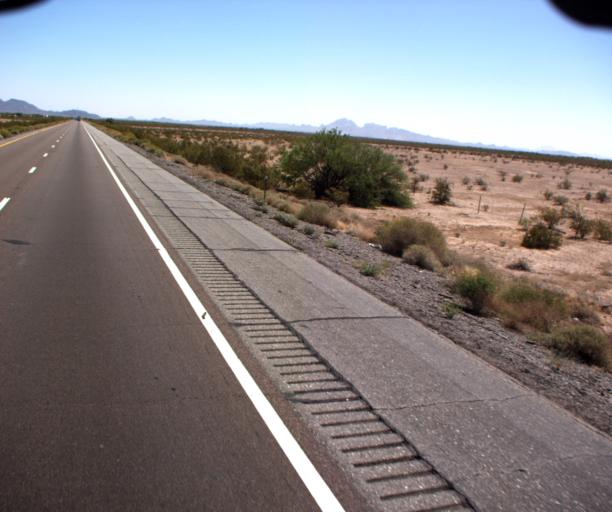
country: US
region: Arizona
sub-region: La Paz County
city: Salome
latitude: 33.5506
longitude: -113.2339
